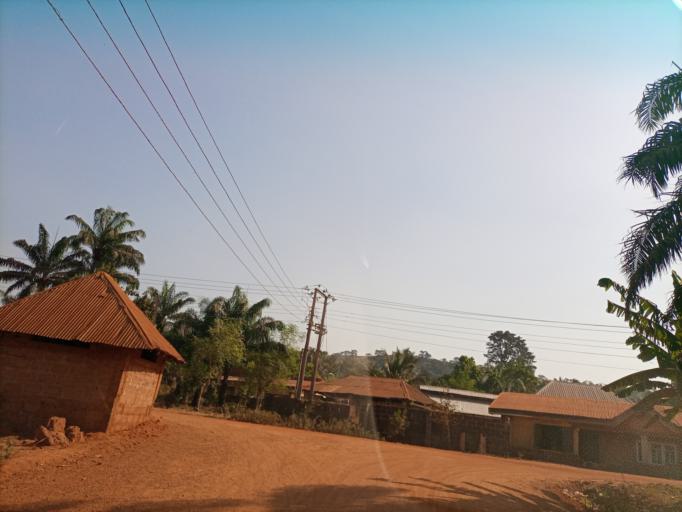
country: NG
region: Enugu
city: Aku
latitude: 6.6989
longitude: 7.3209
